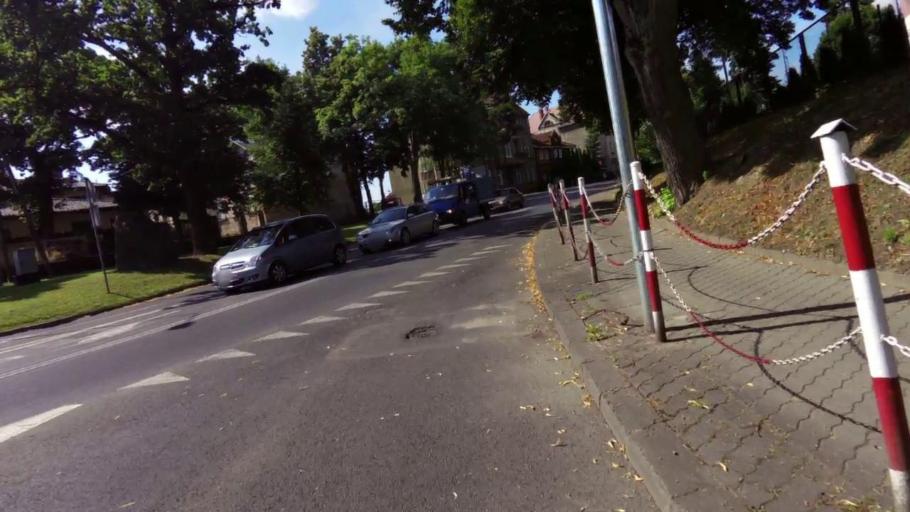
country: PL
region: West Pomeranian Voivodeship
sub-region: Powiat stargardzki
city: Stargard Szczecinski
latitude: 53.3330
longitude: 15.0346
